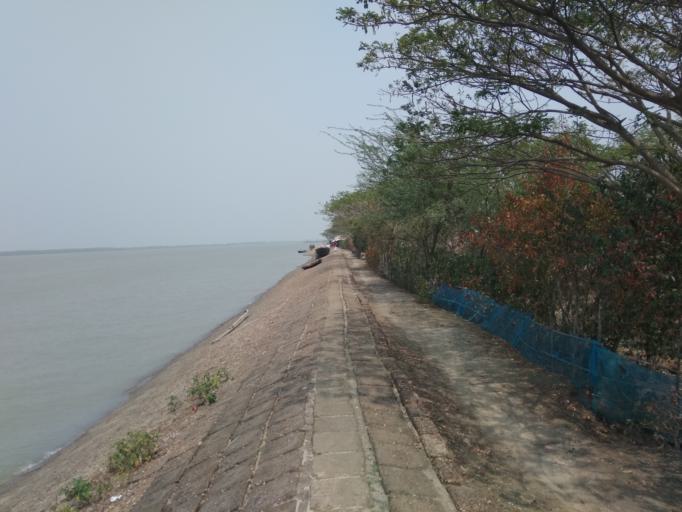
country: IN
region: West Bengal
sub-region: North 24 Parganas
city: Gosaba
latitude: 22.2534
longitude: 89.2505
